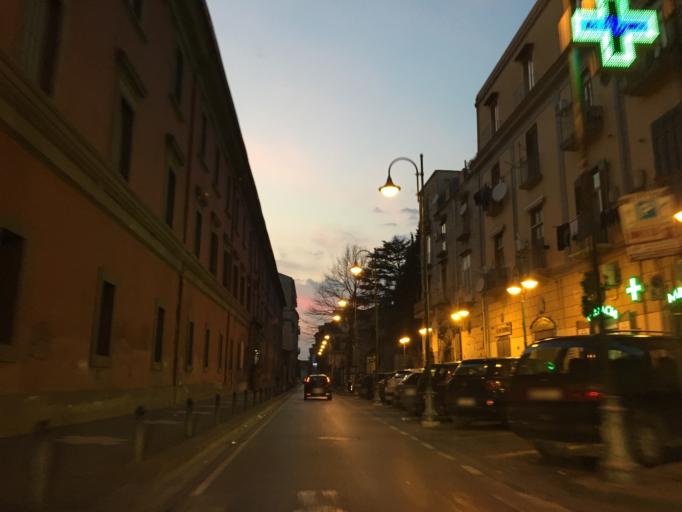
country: IT
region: Campania
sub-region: Provincia di Salerno
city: Nocera Inferiore
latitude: 40.7467
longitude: 14.6436
